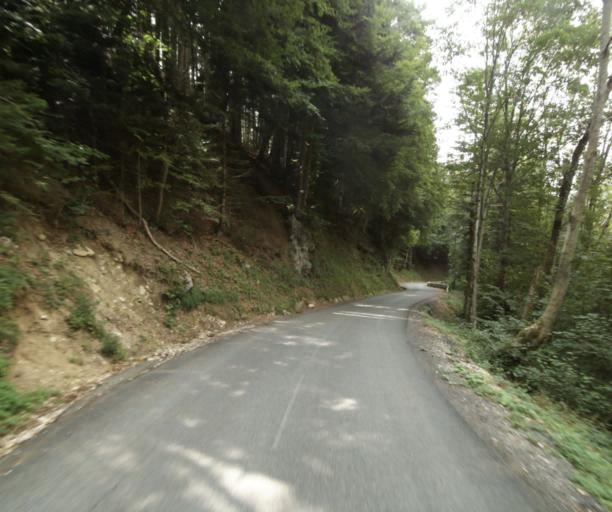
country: FR
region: Rhone-Alpes
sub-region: Departement de l'Isere
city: Le Sappey-en-Chartreuse
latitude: 45.2716
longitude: 5.7549
